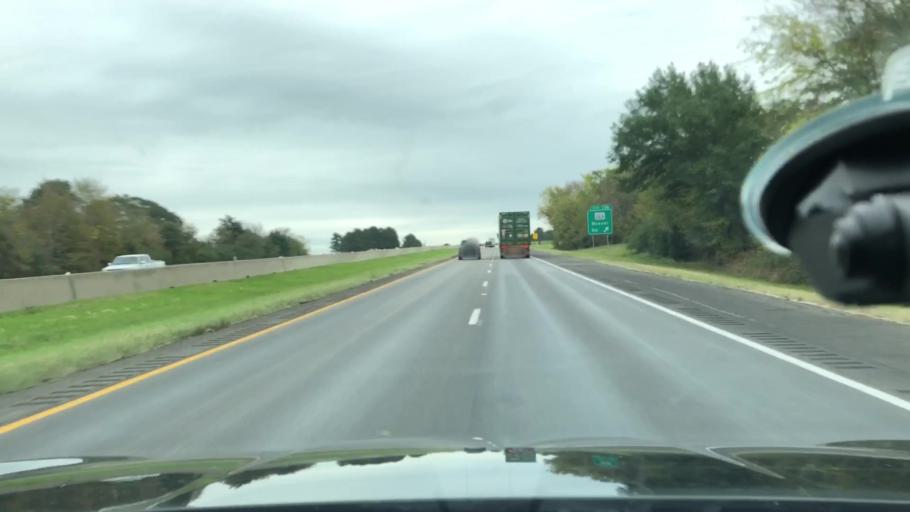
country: US
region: Texas
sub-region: Hopkins County
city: Sulphur Springs
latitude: 33.1599
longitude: -95.4115
